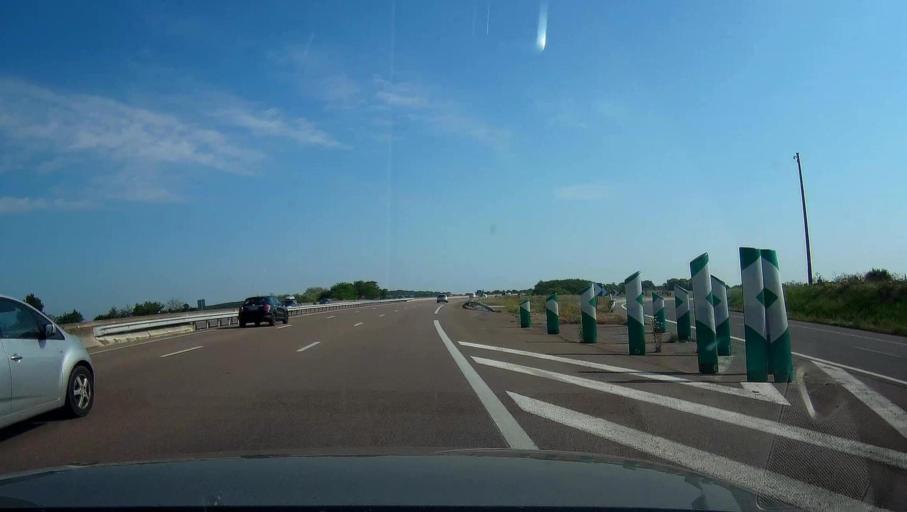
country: FR
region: Bourgogne
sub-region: Departement de la Cote-d'Or
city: Perrigny-les-Dijon
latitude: 47.2384
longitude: 5.0241
